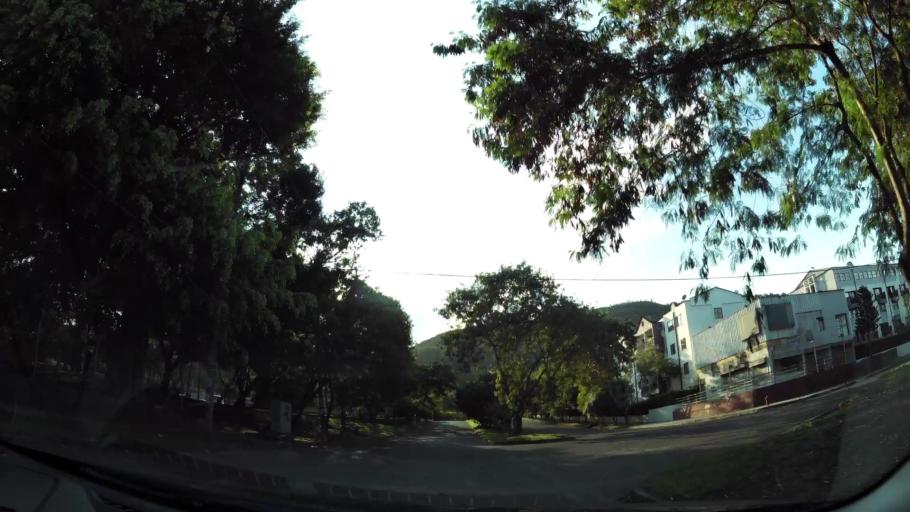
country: CO
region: Valle del Cauca
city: Cali
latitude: 3.4022
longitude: -76.5553
